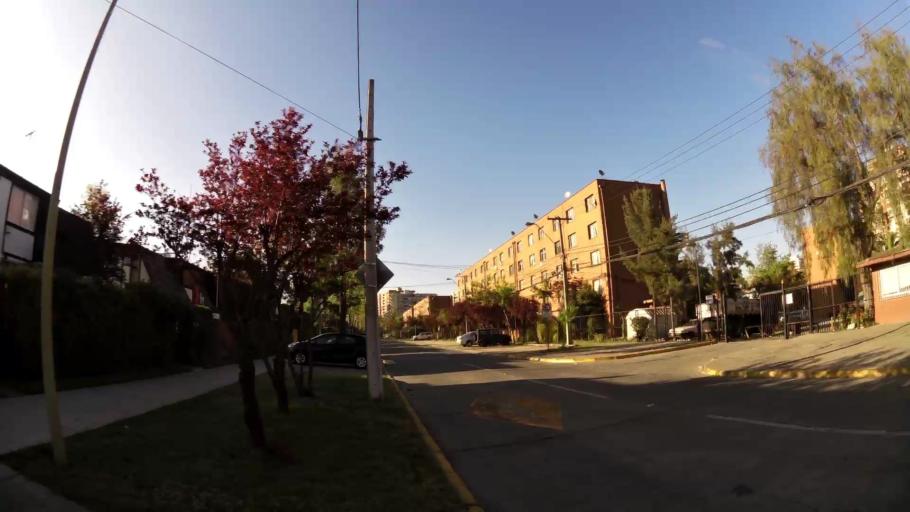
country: CL
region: Santiago Metropolitan
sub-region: Provincia de Santiago
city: Villa Presidente Frei, Nunoa, Santiago, Chile
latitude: -33.4015
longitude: -70.5669
